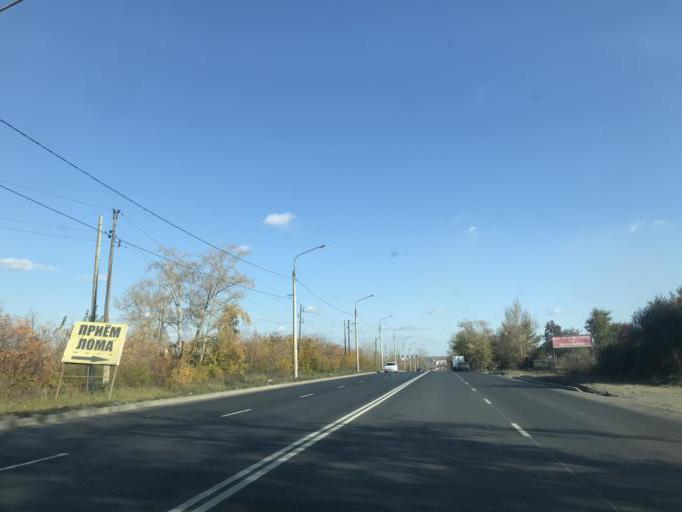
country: RU
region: Chelyabinsk
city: Roshchino
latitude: 55.2406
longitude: 61.3278
